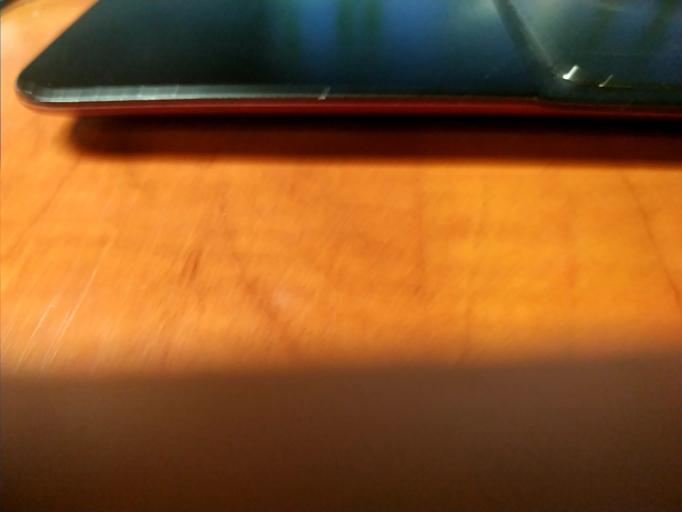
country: RU
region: Smolensk
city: Safonovo
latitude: 55.1842
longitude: 33.0110
